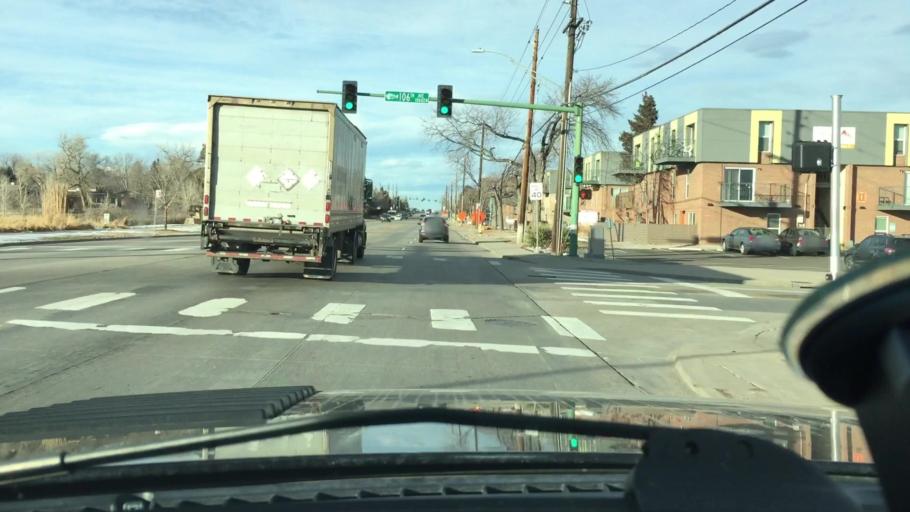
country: US
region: Colorado
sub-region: Adams County
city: Northglenn
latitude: 39.8887
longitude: -104.9966
